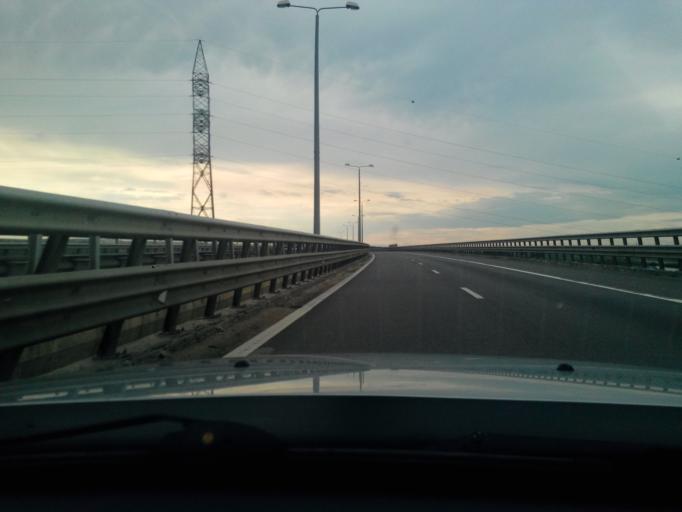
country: RO
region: Arges
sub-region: Oras Stefanesti
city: Golesti
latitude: 44.8263
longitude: 24.9363
